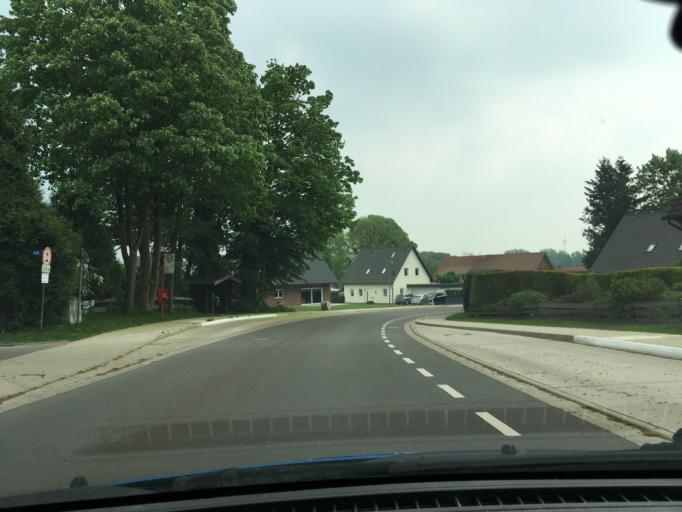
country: DE
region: Lower Saxony
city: Seevetal
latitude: 53.4079
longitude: 9.8974
